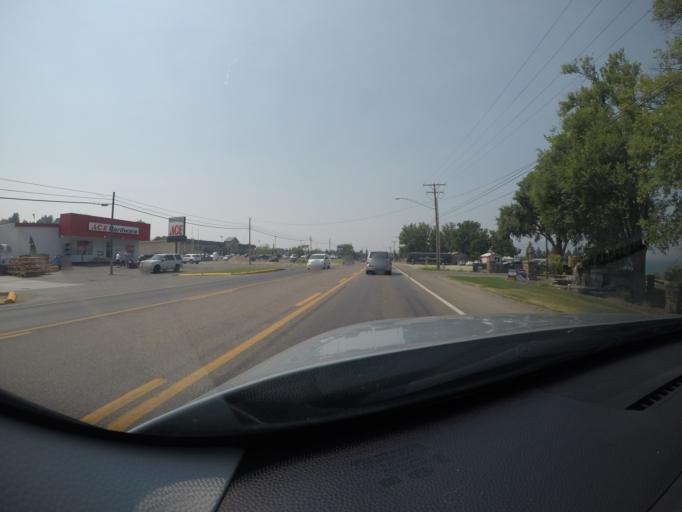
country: US
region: Montana
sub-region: Lake County
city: Polson
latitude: 47.6928
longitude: -114.1431
